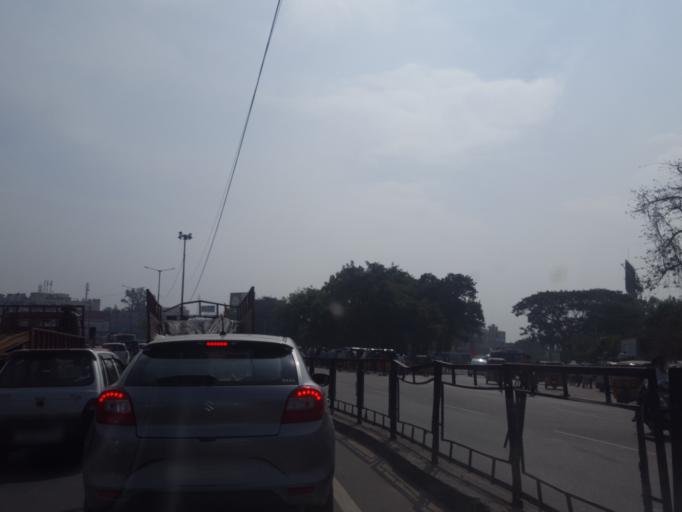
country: IN
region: Telangana
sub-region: Medak
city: Serilingampalle
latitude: 17.4964
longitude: 78.3151
